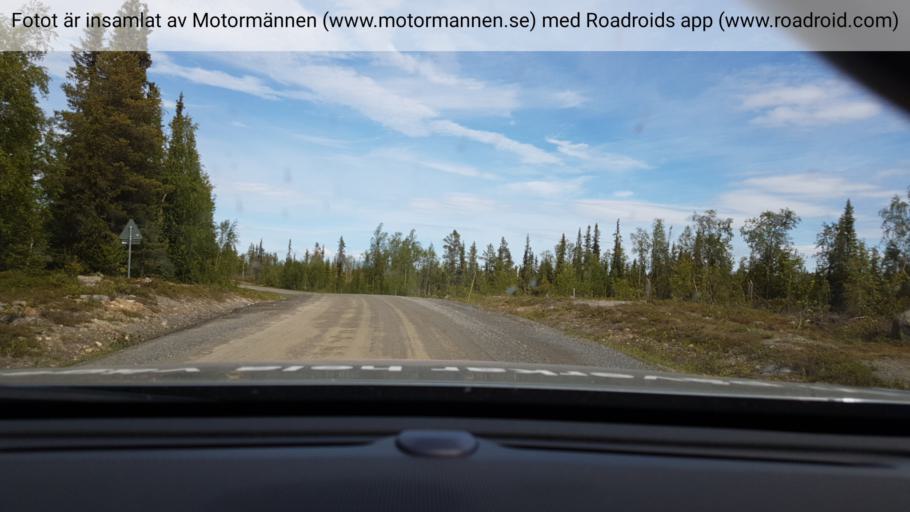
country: SE
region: Vaesterbotten
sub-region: Vilhelmina Kommun
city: Sjoberg
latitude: 65.1647
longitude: 16.3451
